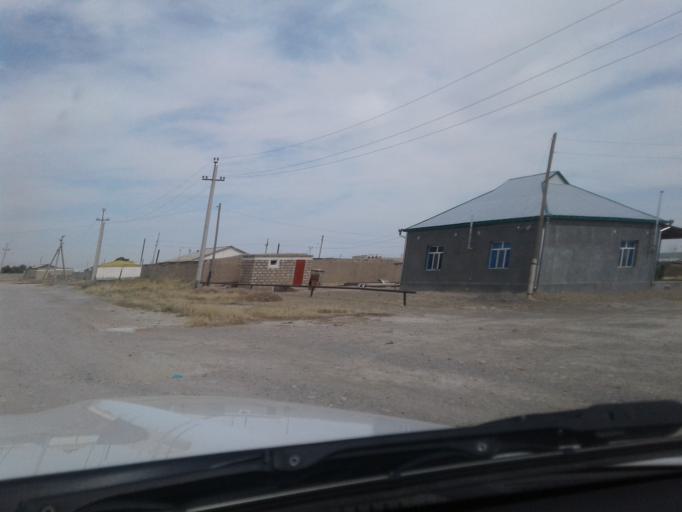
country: TM
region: Balkan
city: Serdar
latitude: 38.9916
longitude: 56.2766
